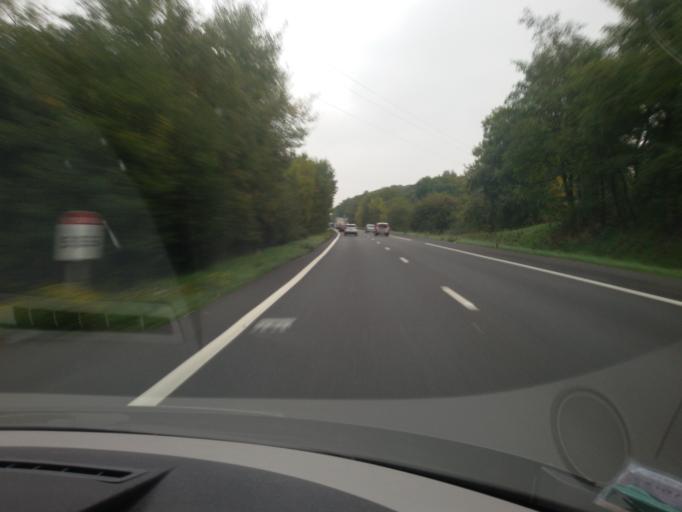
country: FR
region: Ile-de-France
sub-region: Departement de l'Essonne
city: Marcoussis
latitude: 48.6356
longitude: 2.2098
